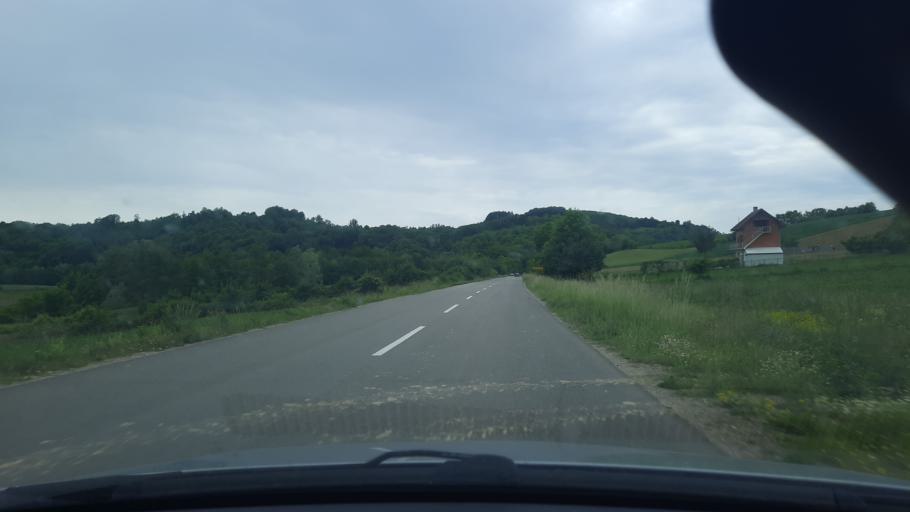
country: RS
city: Bukor
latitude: 44.5172
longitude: 19.5117
